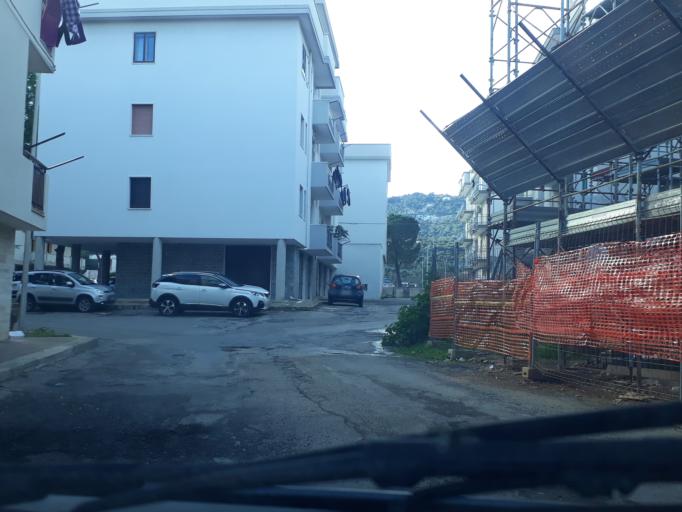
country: IT
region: Apulia
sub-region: Provincia di Brindisi
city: Fasano
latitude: 40.8338
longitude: 17.3545
